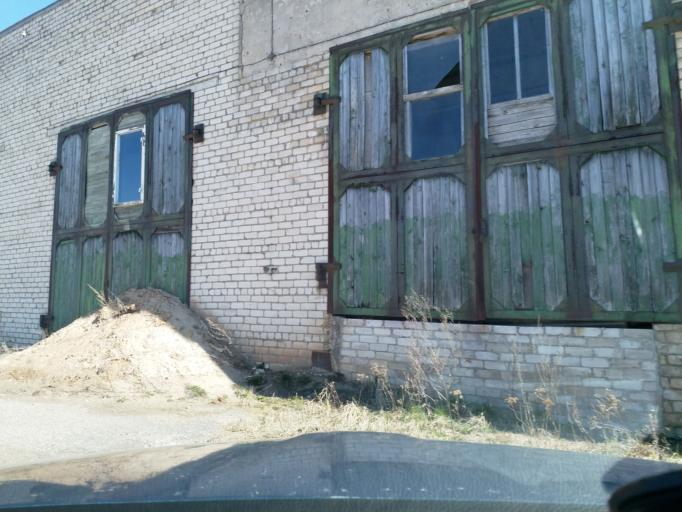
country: LV
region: Kuldigas Rajons
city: Kuldiga
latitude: 56.9968
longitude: 21.8964
